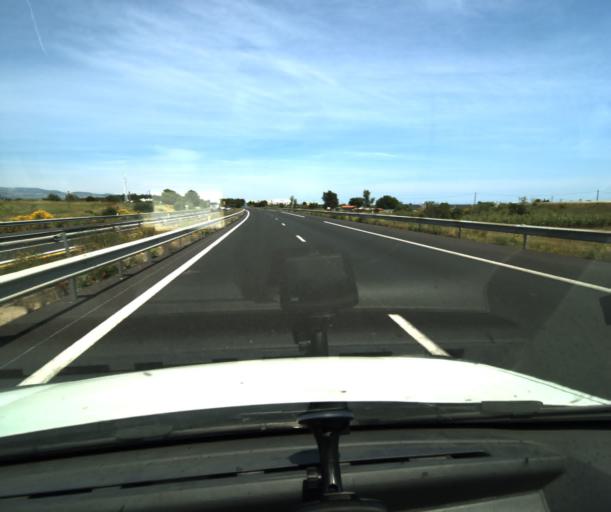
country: FR
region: Languedoc-Roussillon
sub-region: Departement des Pyrenees-Orientales
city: Pia
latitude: 42.7448
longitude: 2.8908
